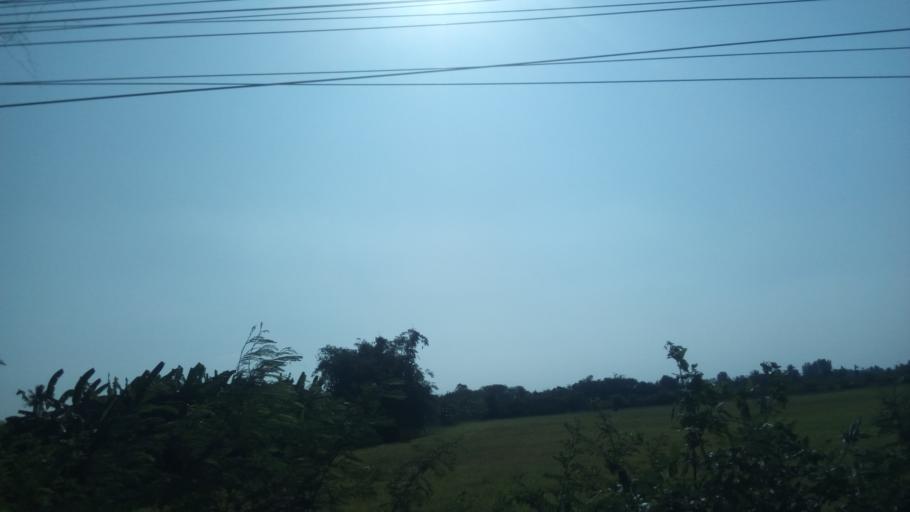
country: TH
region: Nonthaburi
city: Bang Yai
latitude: 13.9037
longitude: 100.3242
